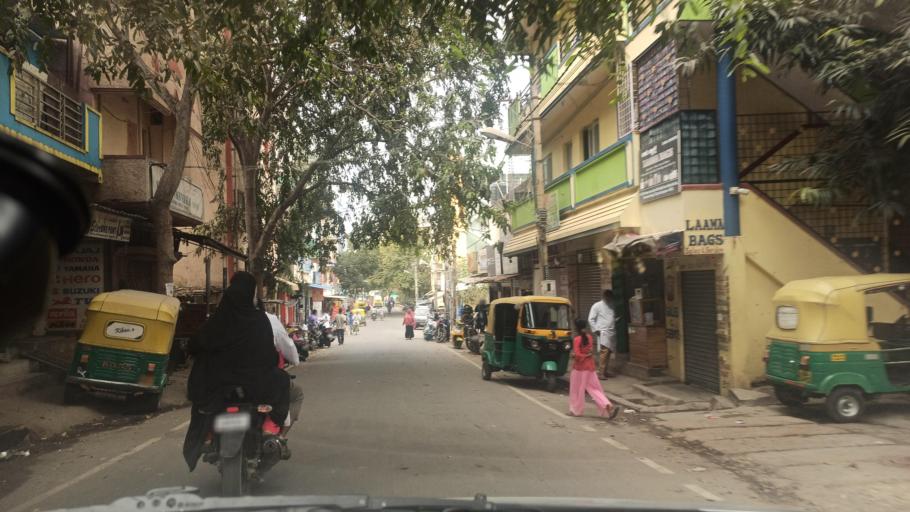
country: IN
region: Karnataka
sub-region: Bangalore Urban
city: Bangalore
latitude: 13.0351
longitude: 77.6035
